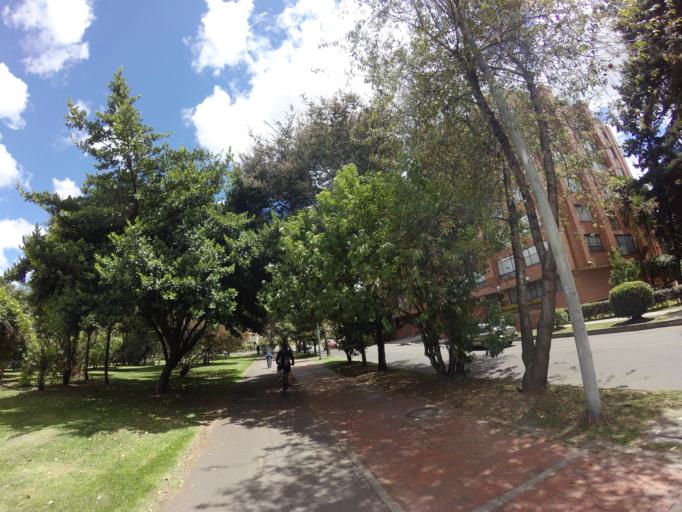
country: CO
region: Bogota D.C.
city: Barrio San Luis
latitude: 4.6980
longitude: -74.0648
